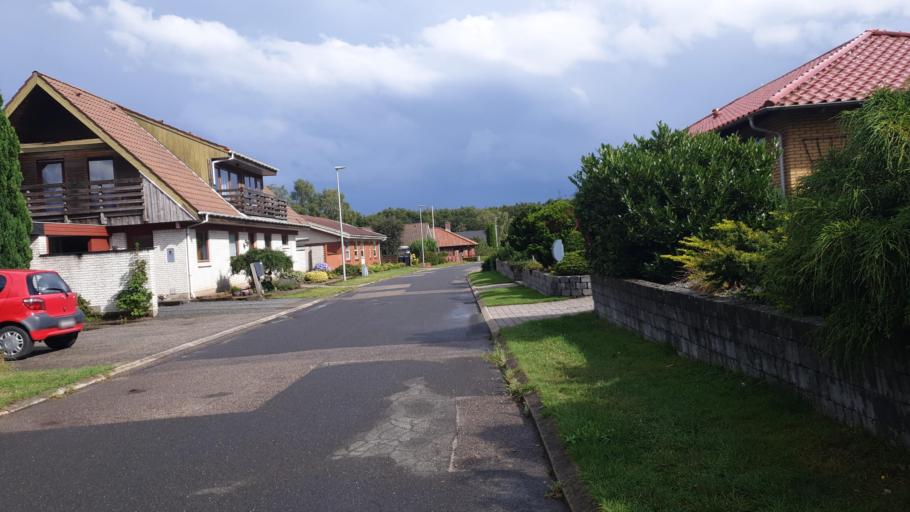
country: DK
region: Central Jutland
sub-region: Silkeborg Kommune
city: Silkeborg
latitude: 56.1919
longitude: 9.5407
